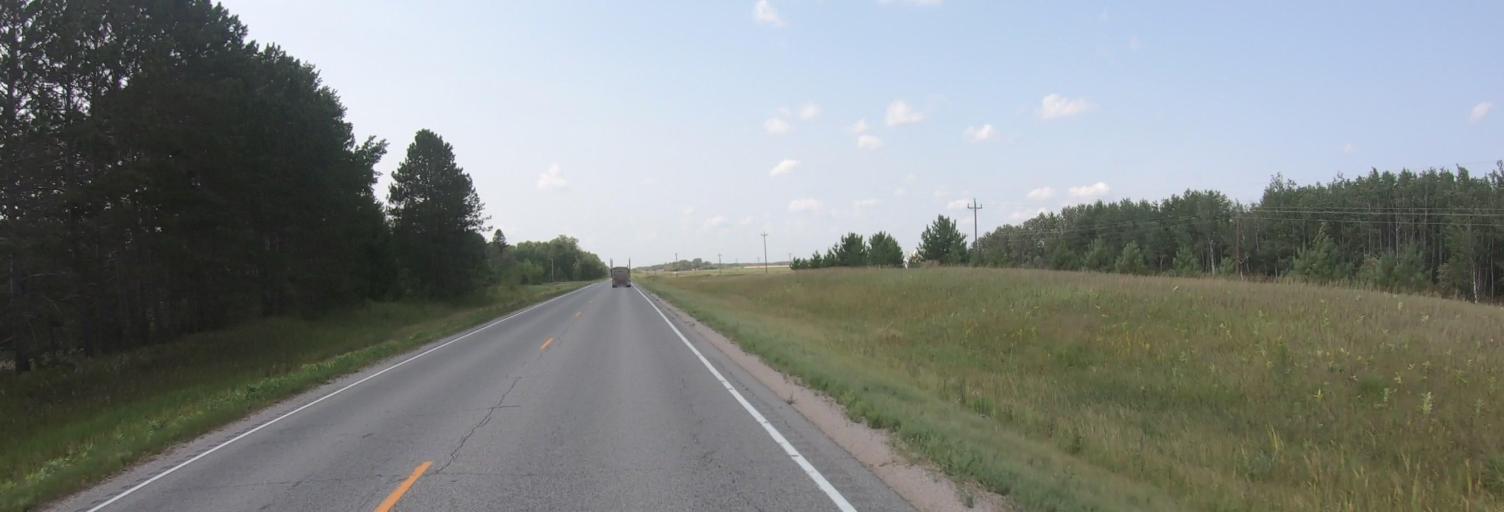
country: US
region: Minnesota
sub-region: Roseau County
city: Warroad
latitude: 48.8382
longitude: -95.1850
